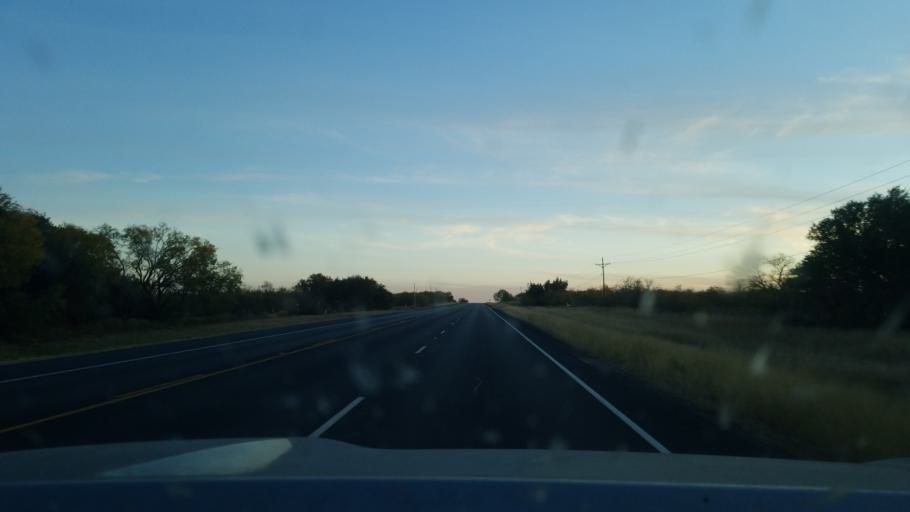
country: US
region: Texas
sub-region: Stephens County
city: Breckenridge
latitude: 32.6867
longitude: -98.9025
